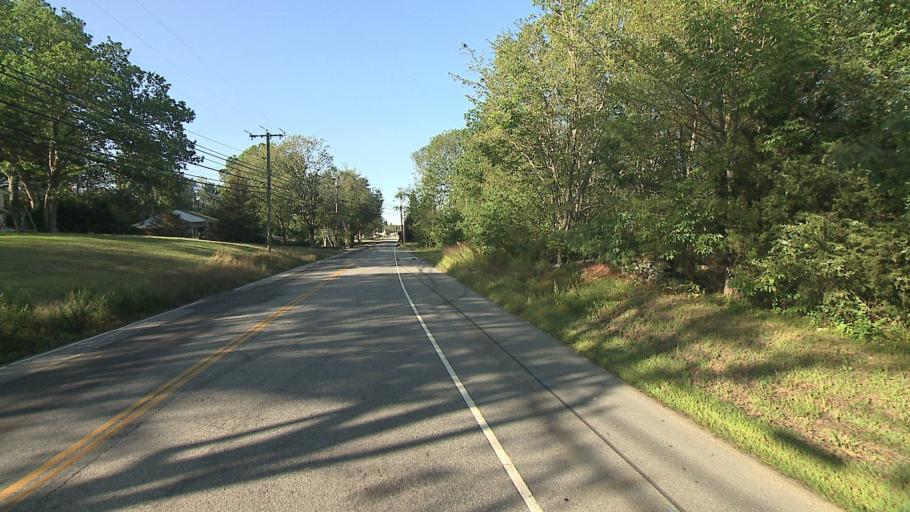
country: US
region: Connecticut
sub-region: Windham County
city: Plainfield Village
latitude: 41.6601
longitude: -71.9250
